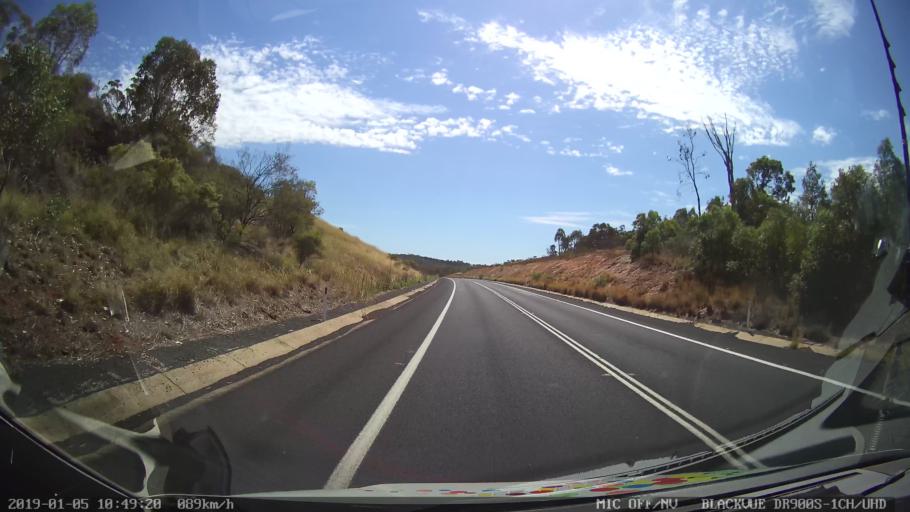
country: AU
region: New South Wales
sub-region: Warrumbungle Shire
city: Coonabarabran
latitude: -31.4348
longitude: 149.0596
